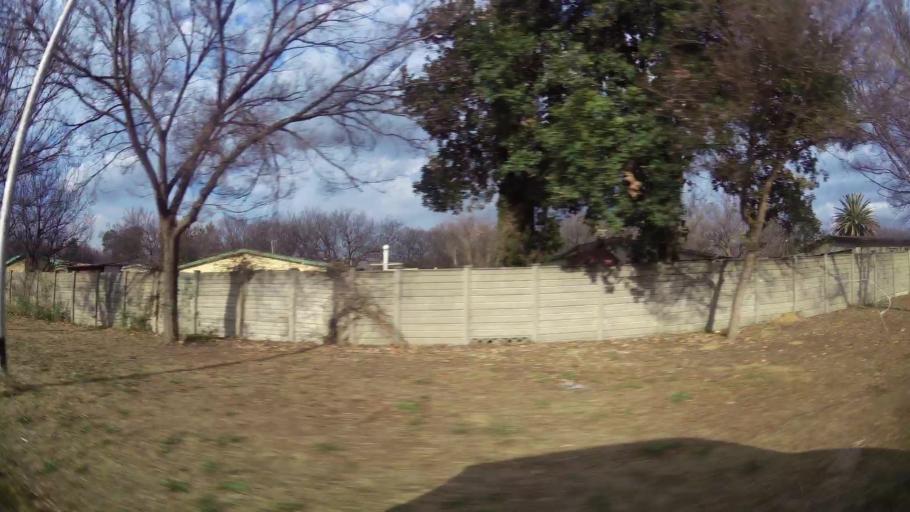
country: ZA
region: Orange Free State
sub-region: Fezile Dabi District Municipality
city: Sasolburg
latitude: -26.8068
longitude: 27.8115
